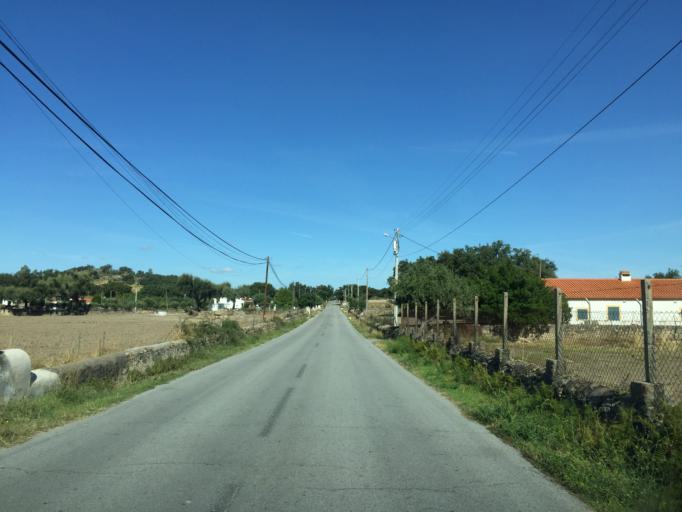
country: PT
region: Portalegre
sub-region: Marvao
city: Marvao
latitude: 39.4271
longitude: -7.3556
